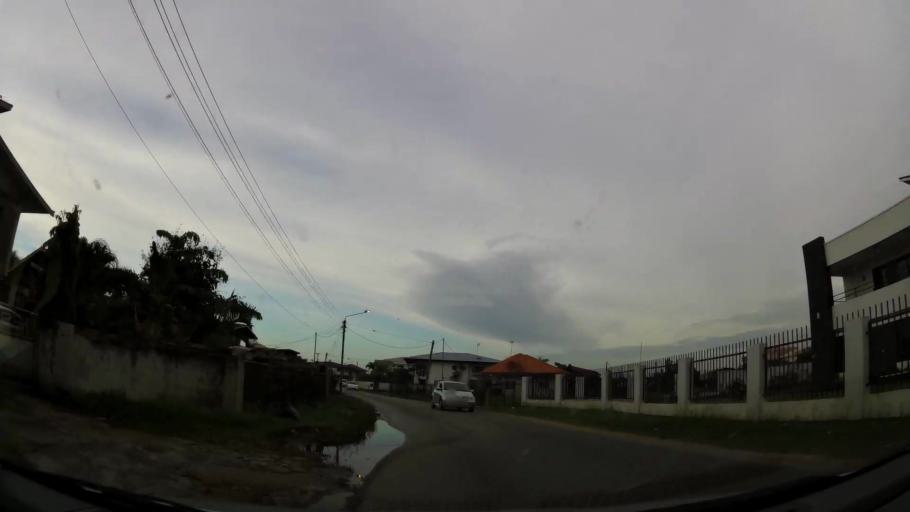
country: SR
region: Paramaribo
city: Paramaribo
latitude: 5.8243
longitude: -55.2043
